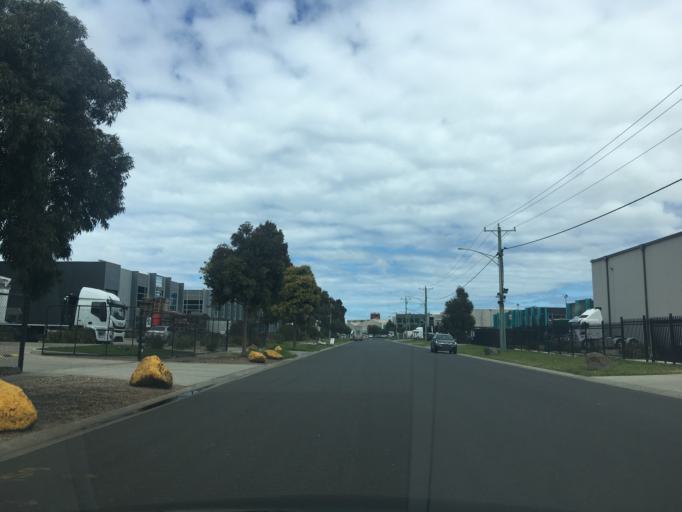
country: AU
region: Victoria
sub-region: Brimbank
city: Sunshine West
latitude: -37.8222
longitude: 144.8015
